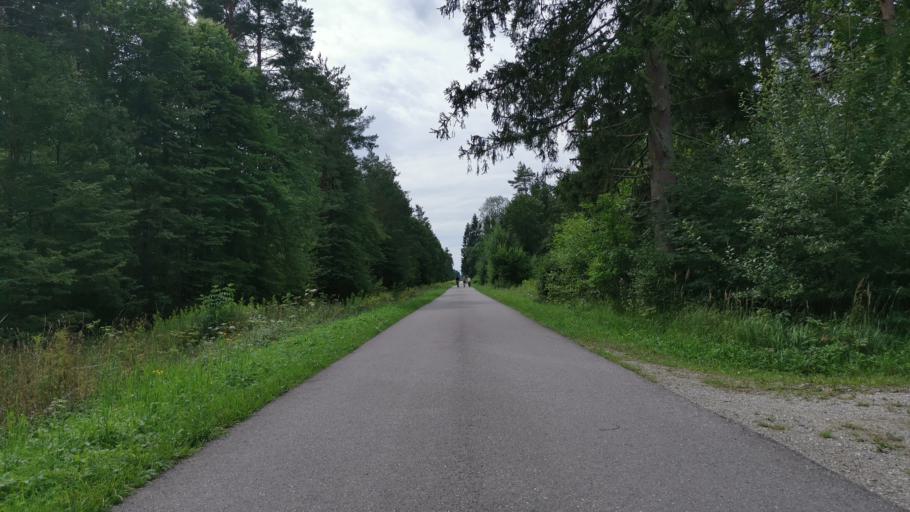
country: DE
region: Bavaria
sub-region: Upper Bavaria
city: Unterhaching
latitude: 48.0765
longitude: 11.5734
